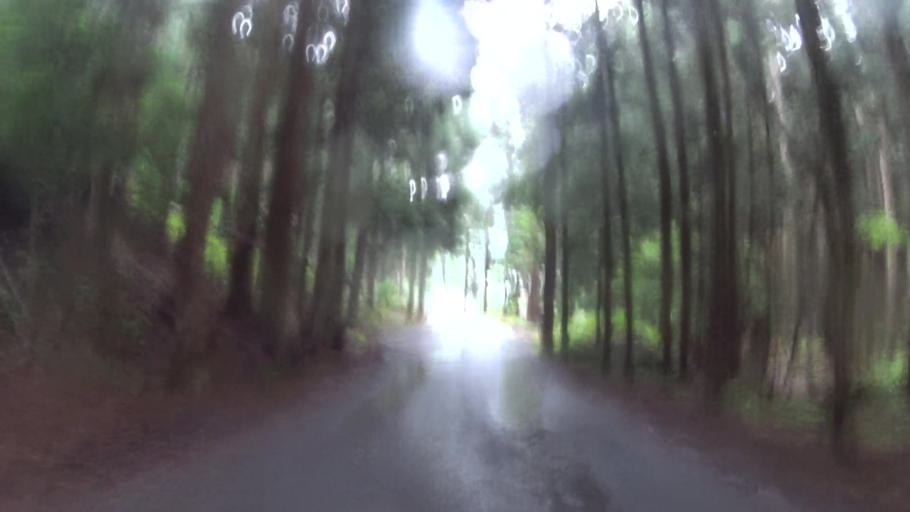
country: JP
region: Shiga Prefecture
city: Kitahama
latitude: 35.2665
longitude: 135.8043
